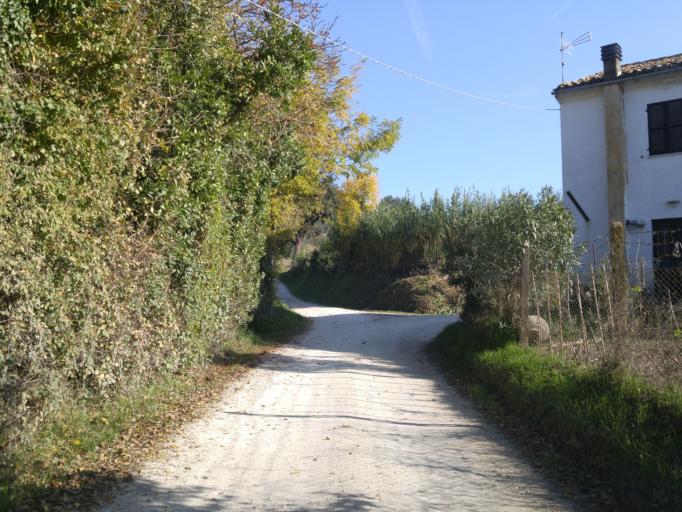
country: IT
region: The Marches
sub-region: Provincia di Pesaro e Urbino
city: Montemaggiore al Metauro
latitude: 43.7320
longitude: 12.9435
